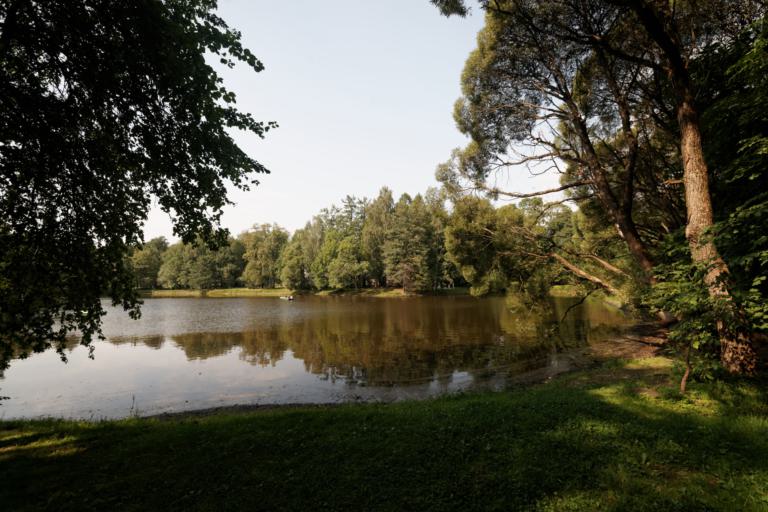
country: RU
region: Leningrad
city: Krestovskiy ostrov
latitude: 59.9806
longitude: 30.2622
